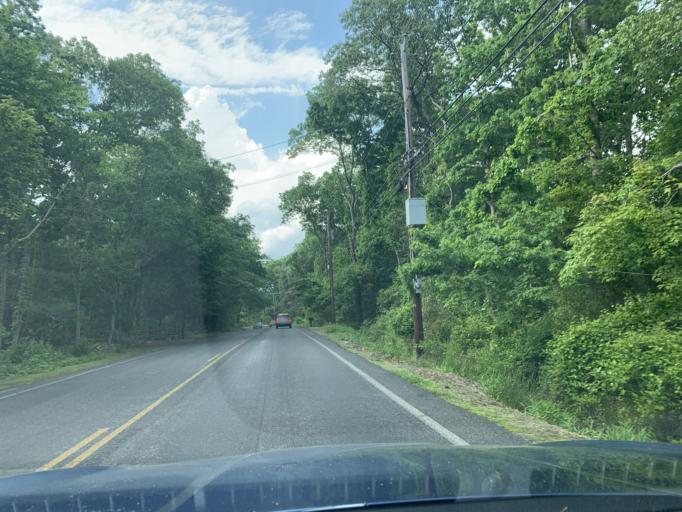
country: US
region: Rhode Island
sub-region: Kent County
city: Coventry
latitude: 41.6837
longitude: -71.6701
